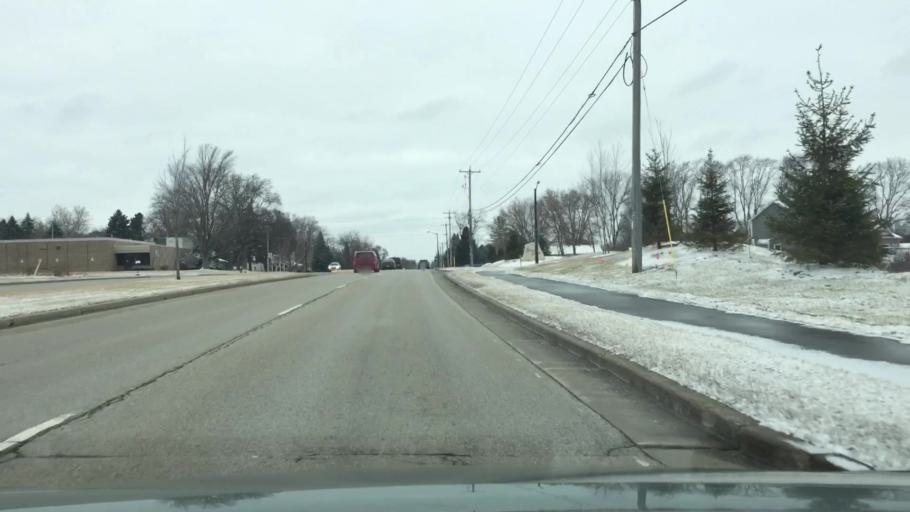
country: US
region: Wisconsin
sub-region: Waukesha County
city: Butler
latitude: 43.1070
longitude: -88.1056
